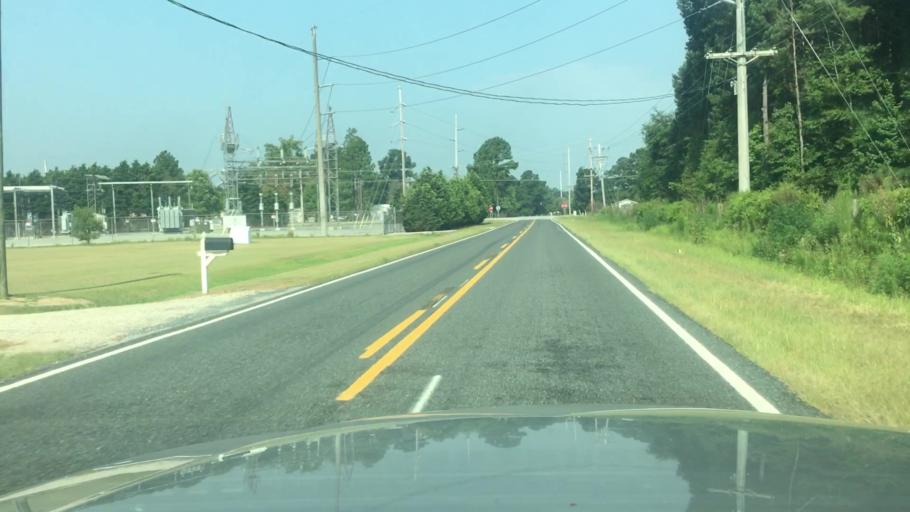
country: US
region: North Carolina
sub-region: Cumberland County
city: Hope Mills
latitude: 34.8984
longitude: -78.8979
